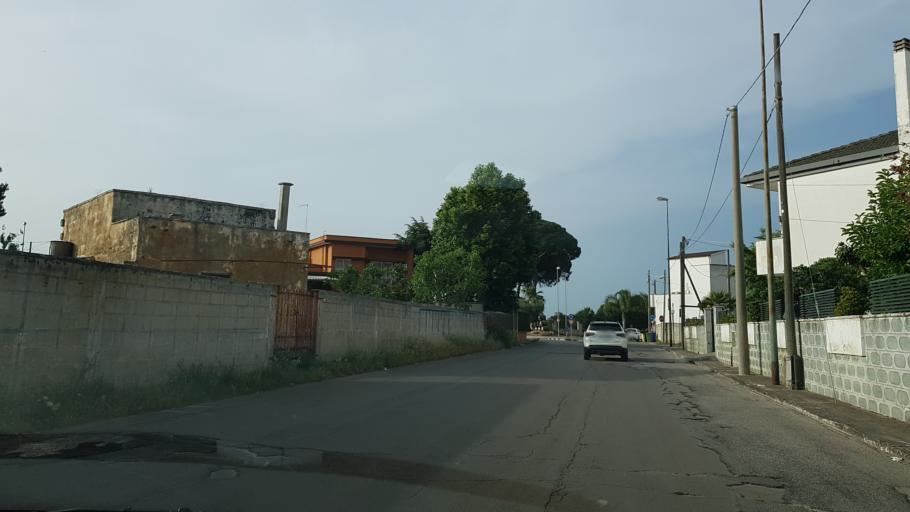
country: IT
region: Apulia
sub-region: Provincia di Brindisi
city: Cellino San Marco
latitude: 40.4735
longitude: 17.9712
